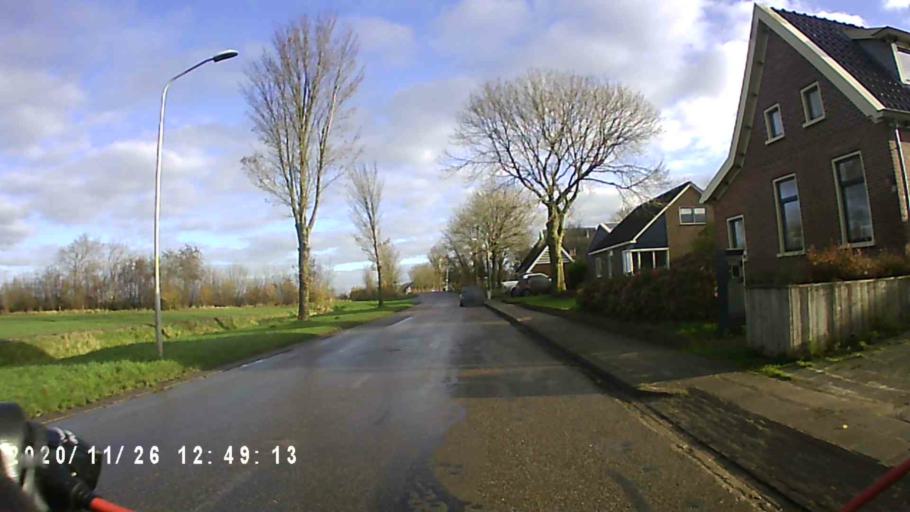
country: NL
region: Groningen
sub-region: Gemeente Appingedam
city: Appingedam
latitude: 53.3481
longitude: 6.7703
